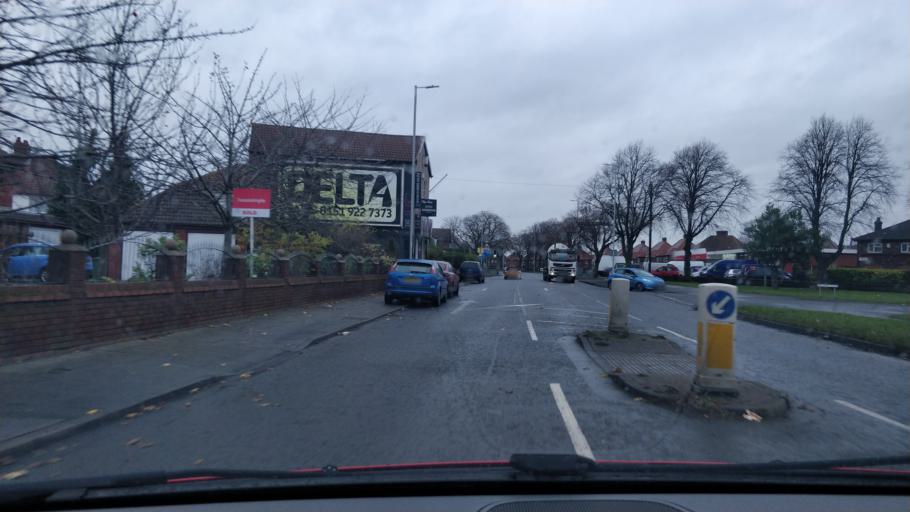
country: GB
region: England
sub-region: Sefton
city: Litherland
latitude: 53.4747
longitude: -2.9972
